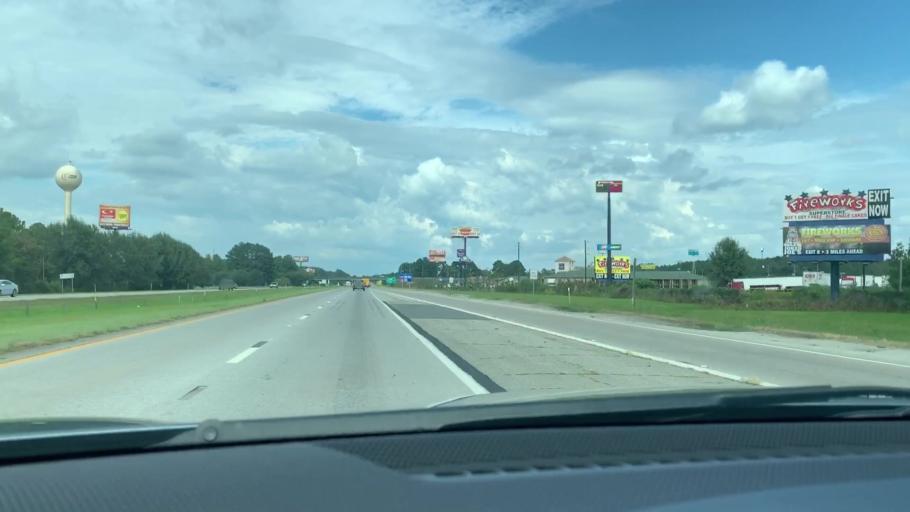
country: US
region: South Carolina
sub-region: Jasper County
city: Hardeeville
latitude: 32.2689
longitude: -81.0852
